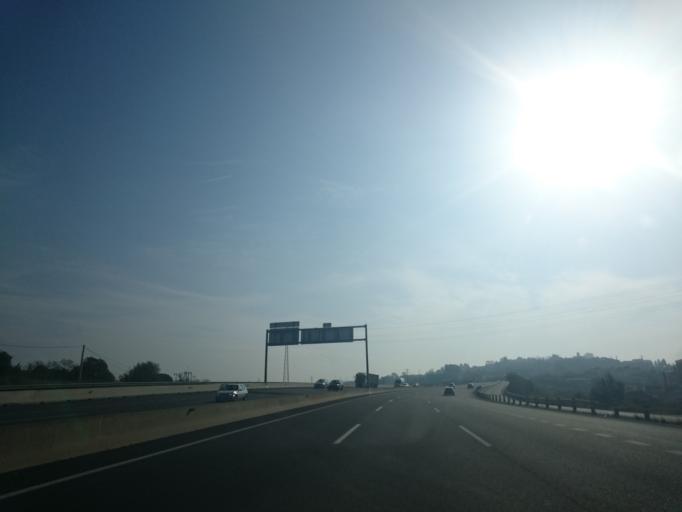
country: ES
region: Catalonia
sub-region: Provincia de Barcelona
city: Sant Joan de Vilatorrada
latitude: 41.7400
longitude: 1.8161
